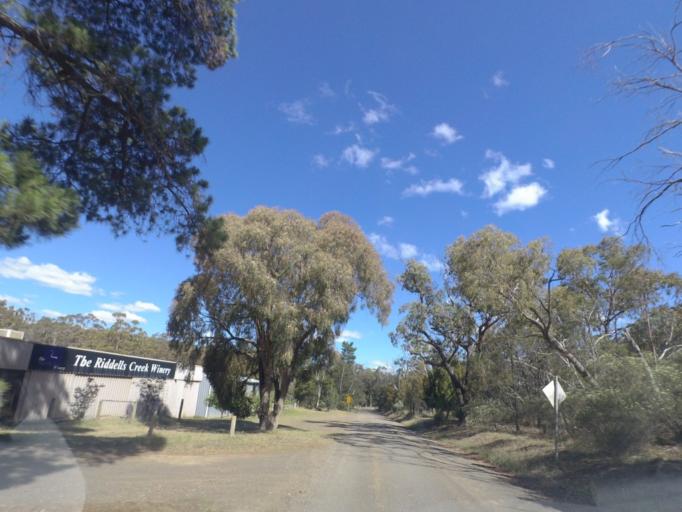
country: AU
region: Victoria
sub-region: Hume
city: Sunbury
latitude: -37.4374
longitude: 144.6641
